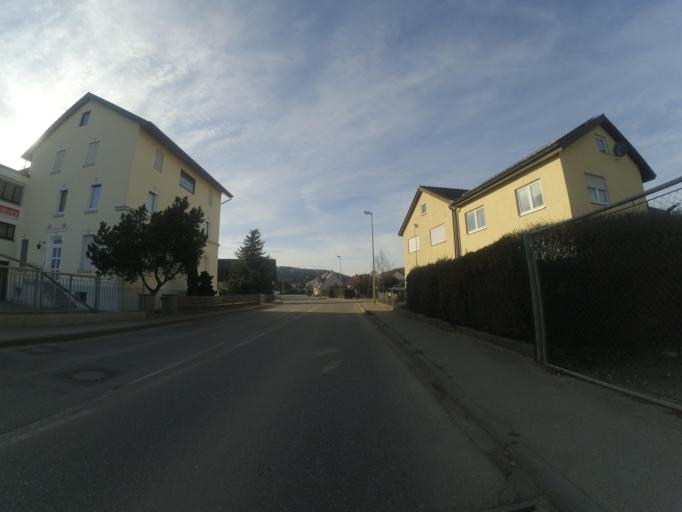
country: DE
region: Baden-Wuerttemberg
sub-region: Regierungsbezirk Stuttgart
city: Bolheim
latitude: 48.6310
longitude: 10.1585
